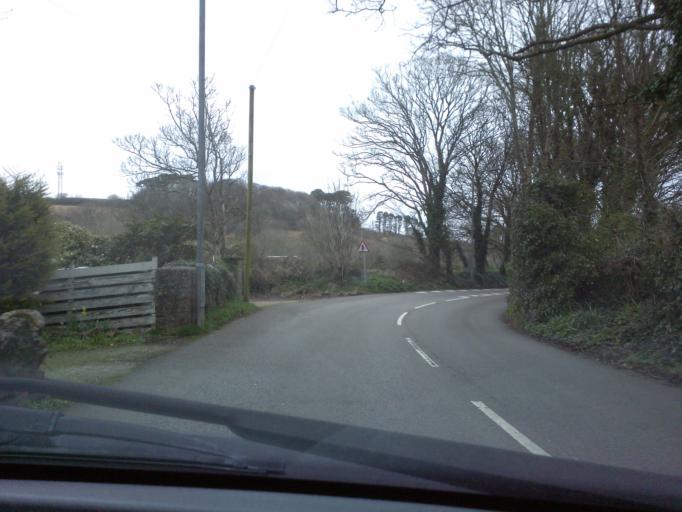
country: GB
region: England
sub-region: Cornwall
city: Penzance
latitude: 50.1094
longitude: -5.5591
